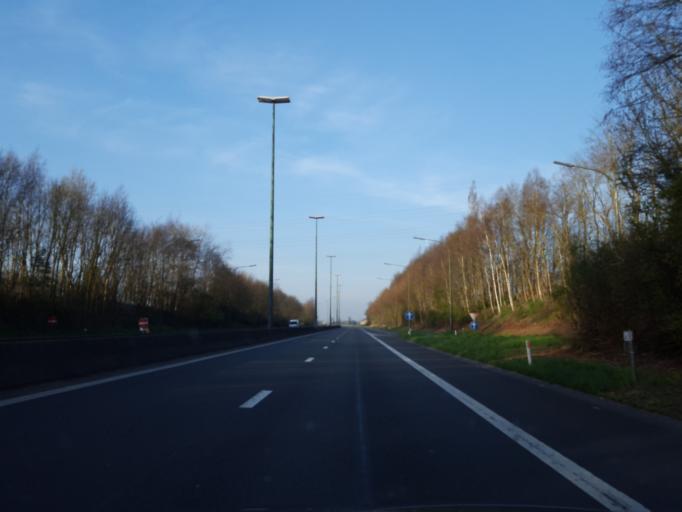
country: BE
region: Wallonia
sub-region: Province du Brabant Wallon
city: Genappe
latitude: 50.6134
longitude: 4.4015
